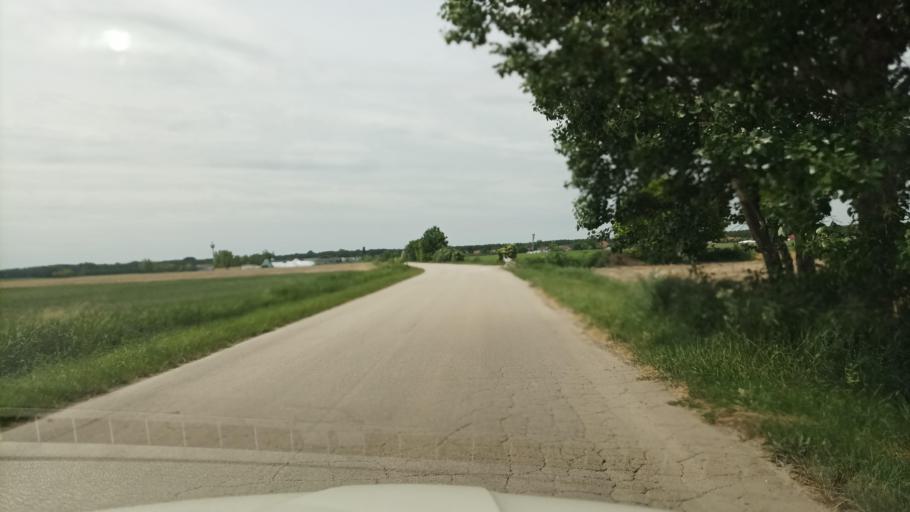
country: HU
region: Fejer
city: Adony
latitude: 47.1194
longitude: 18.9107
